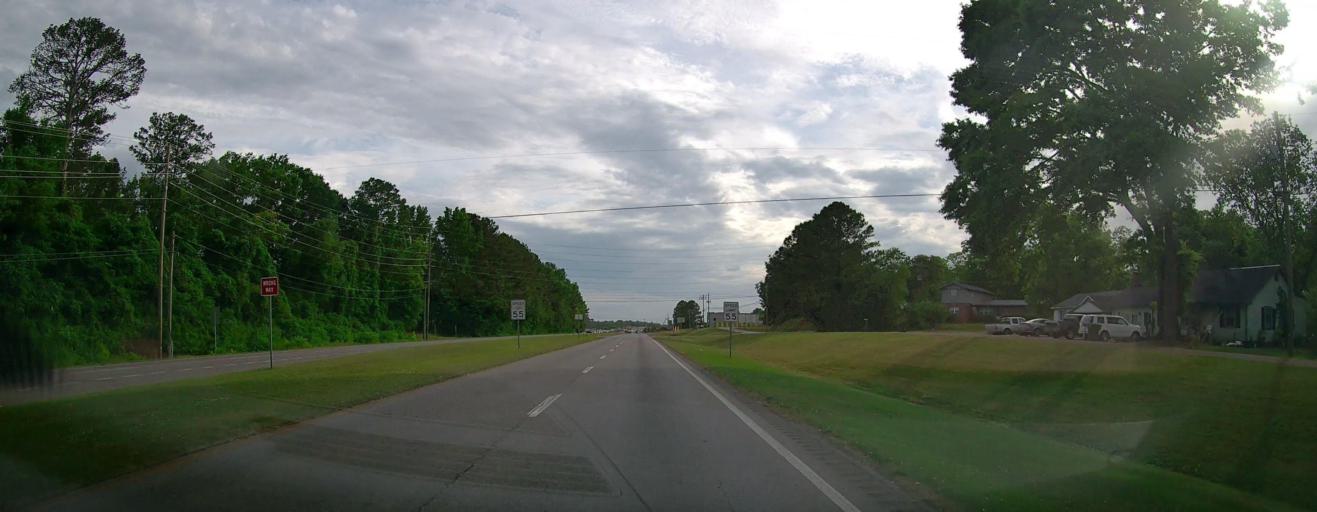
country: US
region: Alabama
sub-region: Calhoun County
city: Oxford
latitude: 33.5998
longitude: -85.8372
